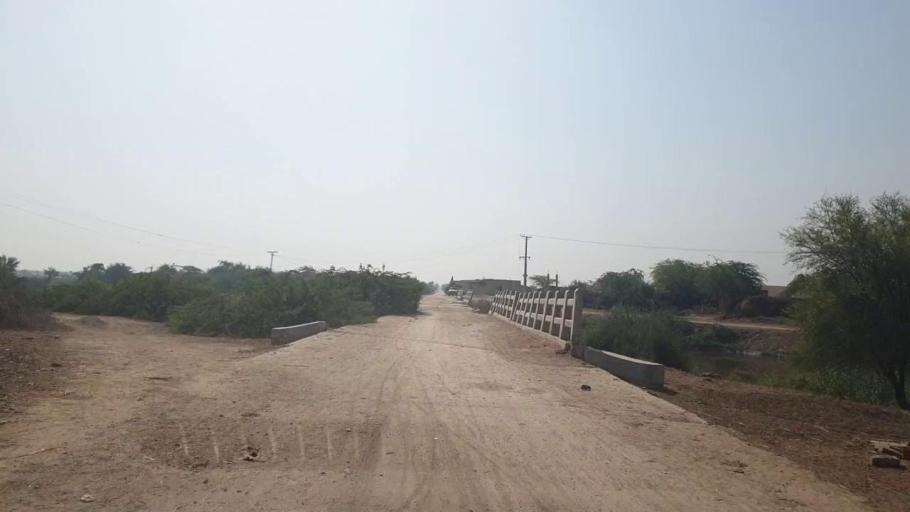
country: PK
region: Sindh
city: Shahdadpur
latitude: 25.9075
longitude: 68.7432
